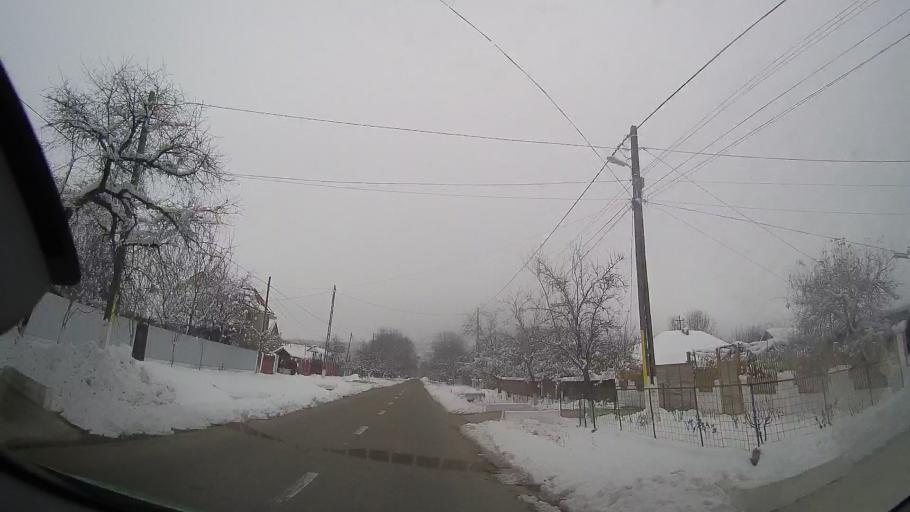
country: RO
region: Vaslui
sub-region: Comuna Bacesti
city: Bacesti
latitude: 46.8212
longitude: 27.2024
